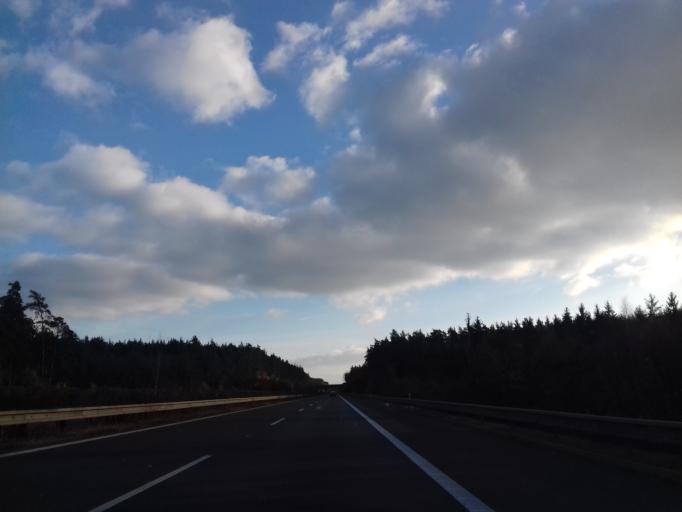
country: CZ
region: Plzensky
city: Vejprnice
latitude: 49.7009
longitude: 13.2906
